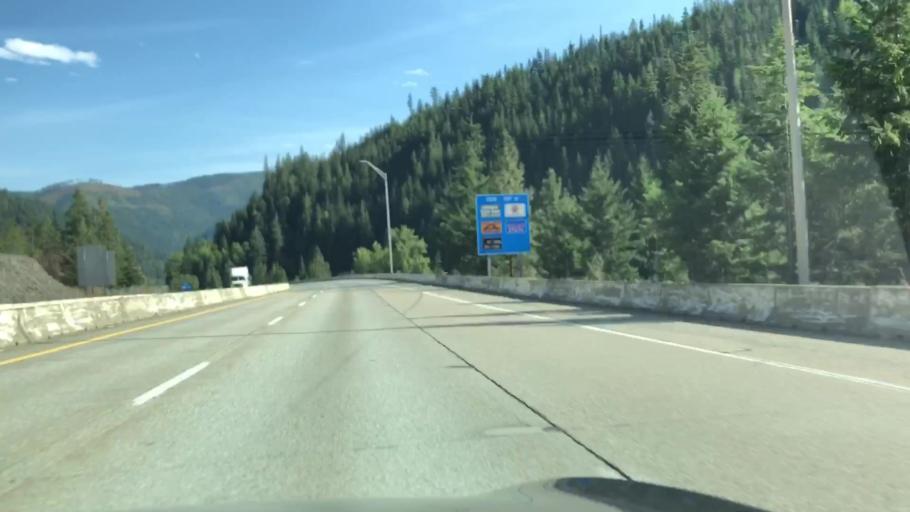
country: US
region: Idaho
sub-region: Shoshone County
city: Wallace
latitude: 47.4895
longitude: -115.9513
